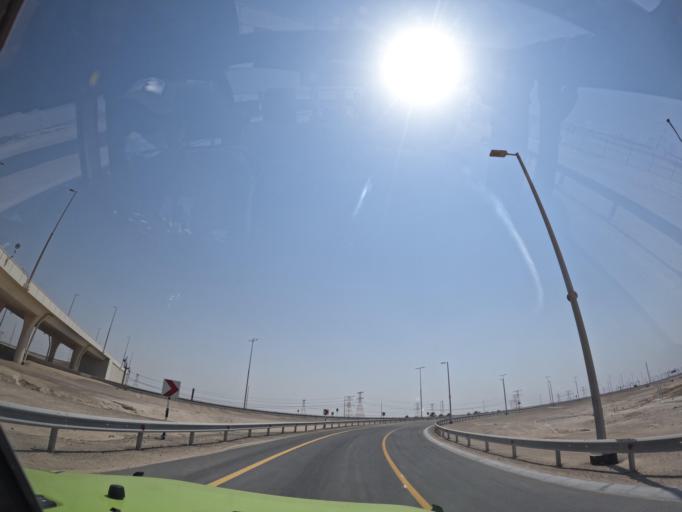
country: AE
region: Abu Dhabi
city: Abu Dhabi
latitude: 24.1641
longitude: 54.3539
